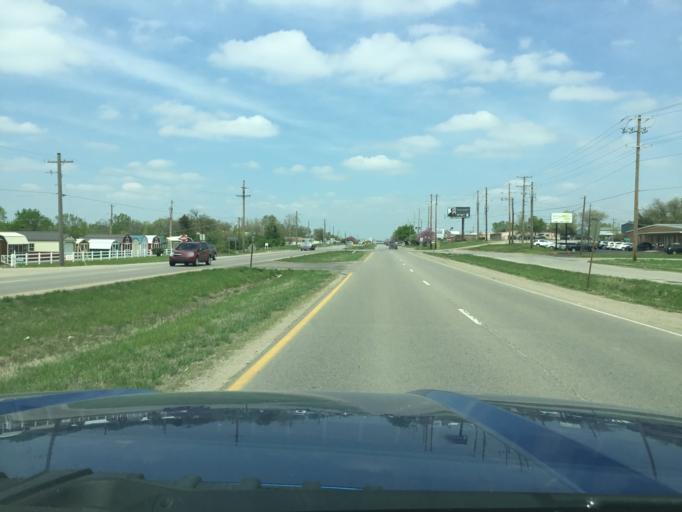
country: US
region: Kansas
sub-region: Shawnee County
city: Topeka
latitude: 38.9776
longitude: -95.6876
